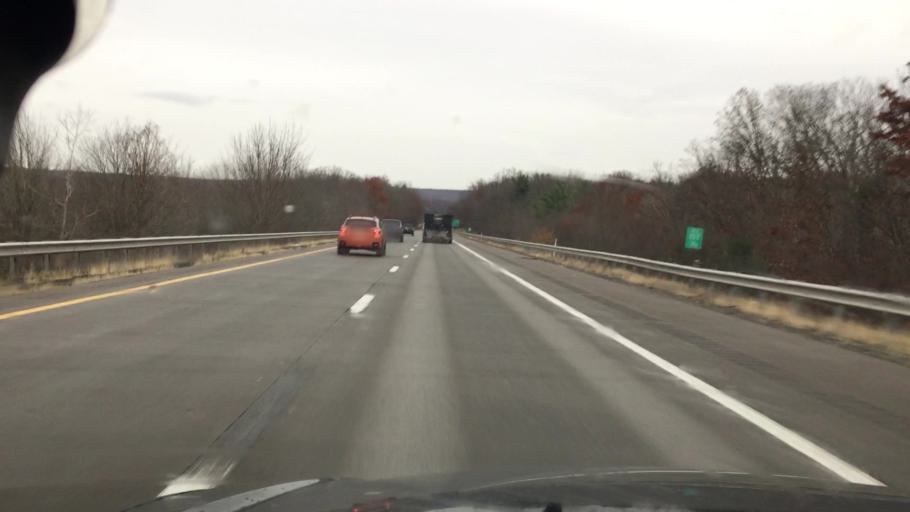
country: US
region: Pennsylvania
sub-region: Luzerne County
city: Nanticoke
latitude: 41.1261
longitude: -75.9618
